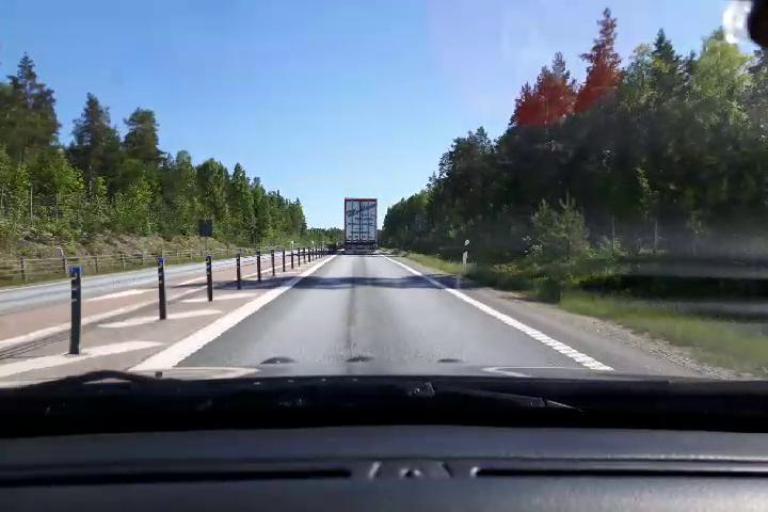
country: SE
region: Gaevleborg
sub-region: Soderhamns Kommun
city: Soderhamn
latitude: 61.2630
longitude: 17.0318
